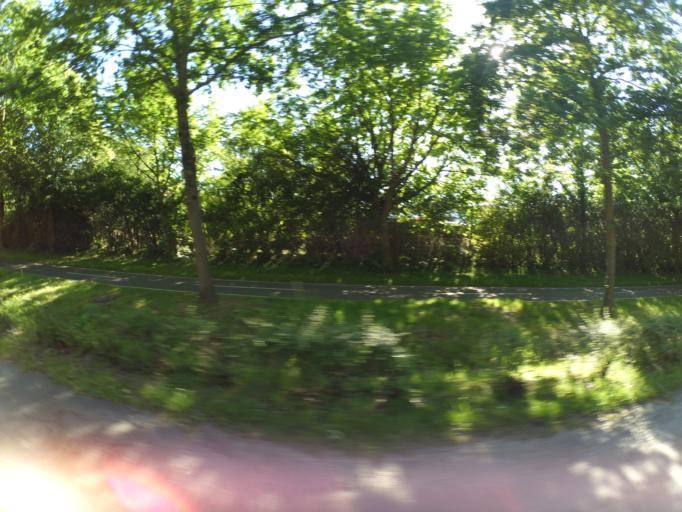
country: FR
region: Pays de la Loire
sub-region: Departement de la Vendee
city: Les Herbiers
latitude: 46.8686
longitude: -1.0268
